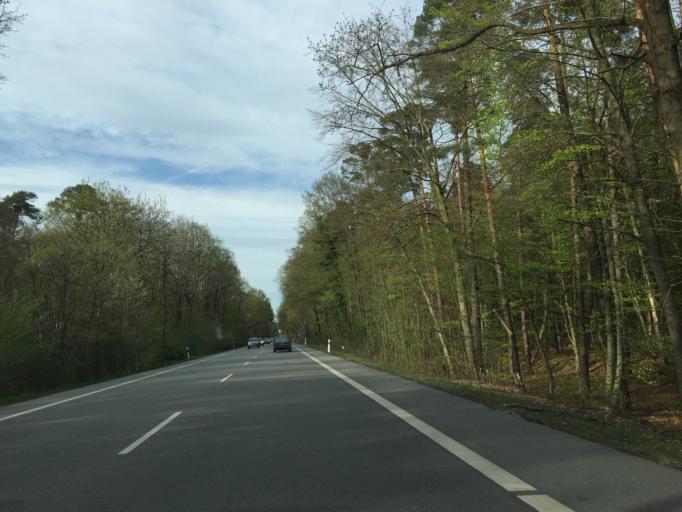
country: DE
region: Hesse
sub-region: Regierungsbezirk Darmstadt
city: Seeheim-Jugenheim
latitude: 49.7883
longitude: 8.6331
